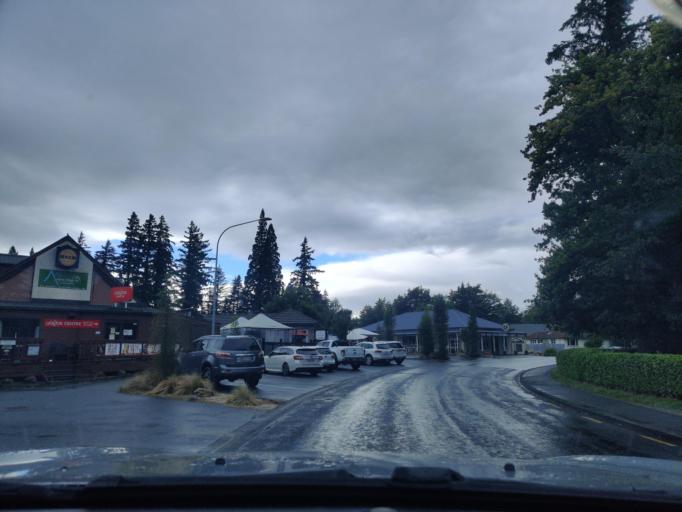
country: NZ
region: Canterbury
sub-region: Hurunui District
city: Amberley
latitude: -42.5211
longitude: 172.8279
